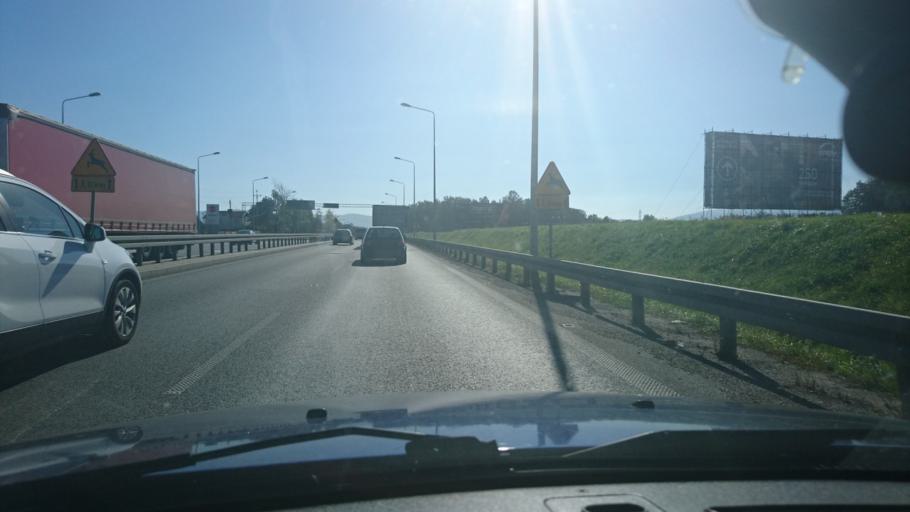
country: PL
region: Silesian Voivodeship
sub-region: Powiat bielski
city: Mazancowice
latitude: 49.8713
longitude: 19.0050
